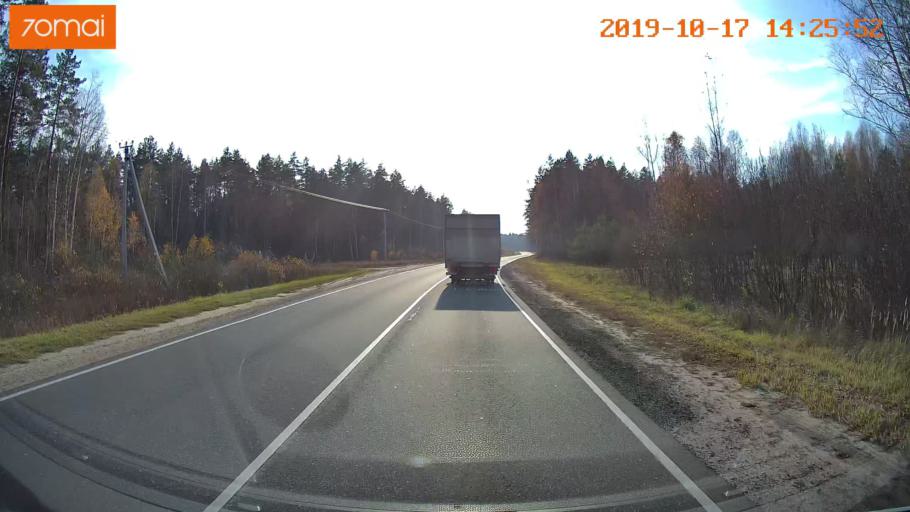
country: RU
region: Moskovskaya
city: Radovitskiy
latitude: 54.9965
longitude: 39.9742
